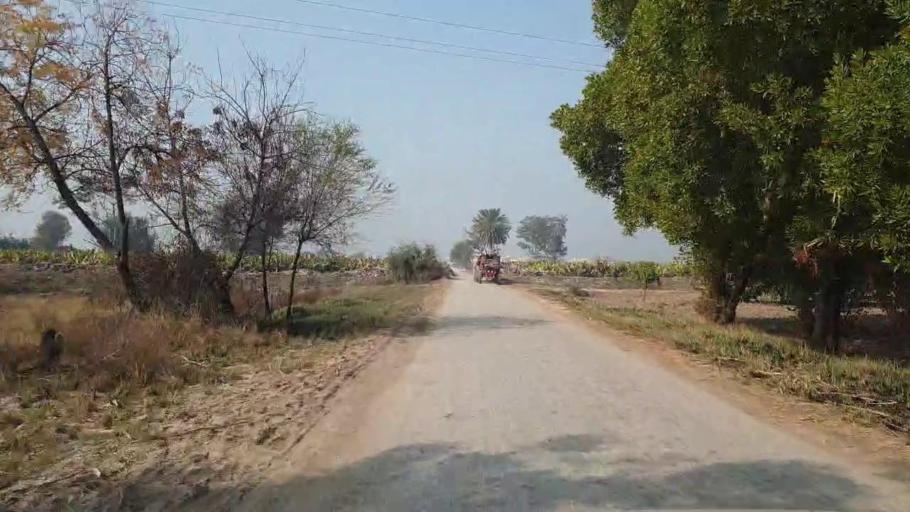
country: PK
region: Sindh
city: Sakrand
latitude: 25.9917
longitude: 68.3644
